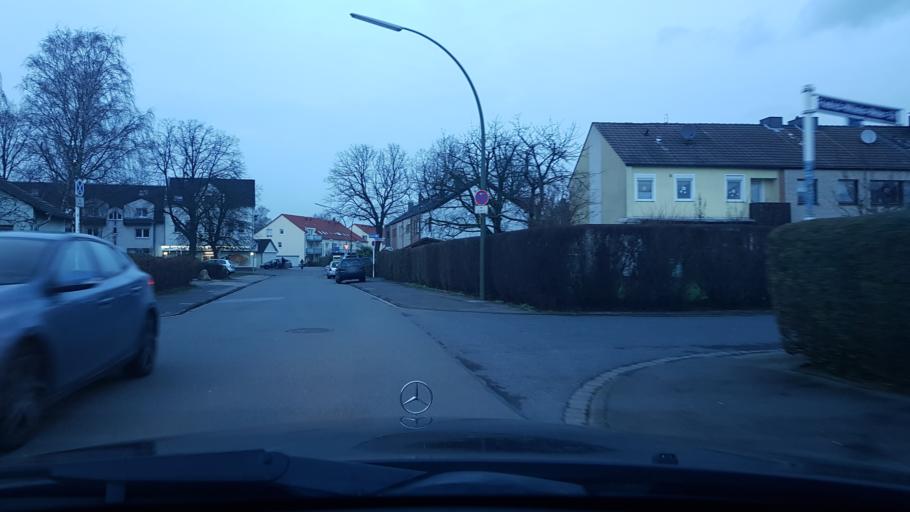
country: DE
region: North Rhine-Westphalia
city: Marl
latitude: 51.6583
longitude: 7.0759
